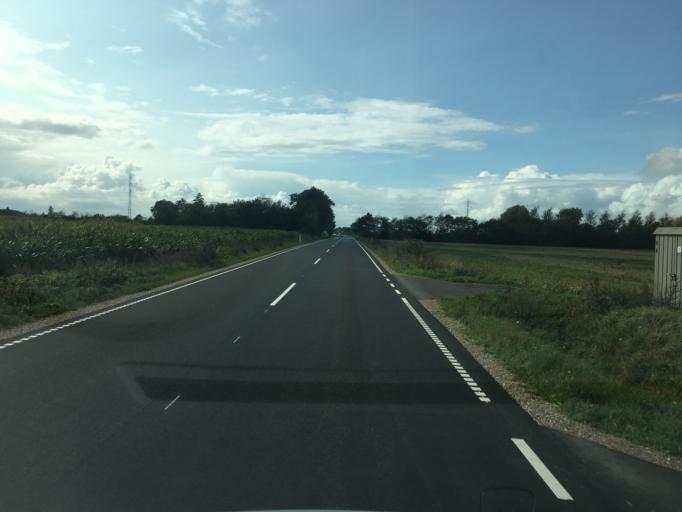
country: DK
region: South Denmark
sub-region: Tonder Kommune
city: Tonder
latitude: 55.0147
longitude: 8.8679
